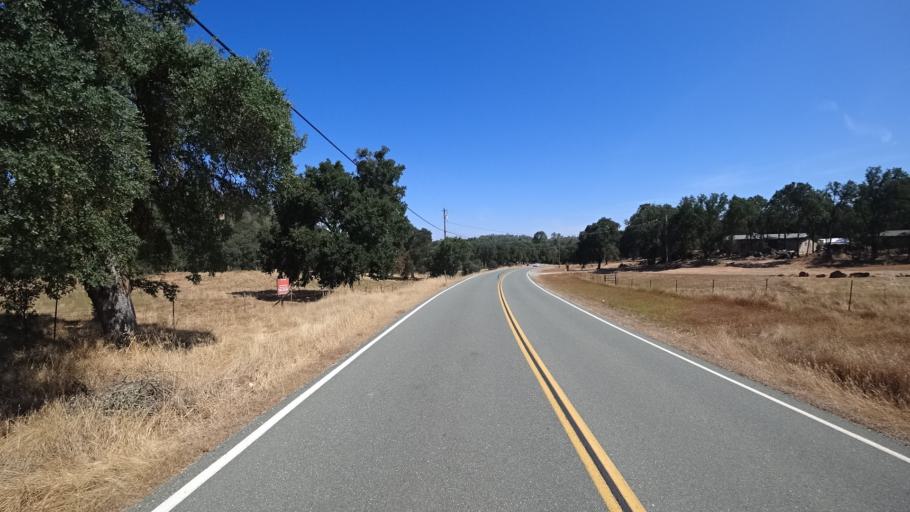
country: US
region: California
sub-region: Calaveras County
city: Valley Springs
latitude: 38.2100
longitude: -120.8802
